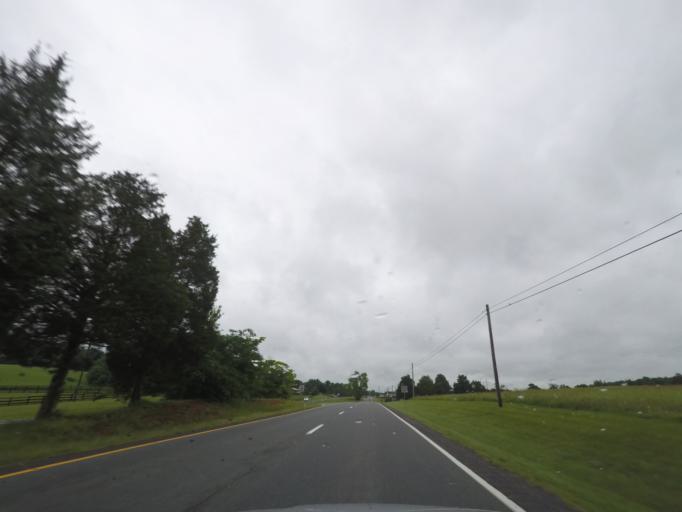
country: US
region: Virginia
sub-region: Orange County
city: Orange
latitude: 38.2154
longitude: -78.1308
